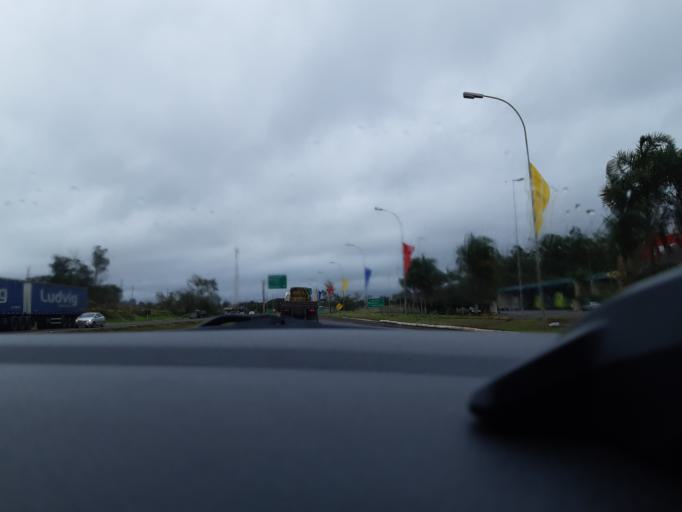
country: BR
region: Sao Paulo
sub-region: Ourinhos
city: Ourinhos
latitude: -22.9809
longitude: -49.9035
